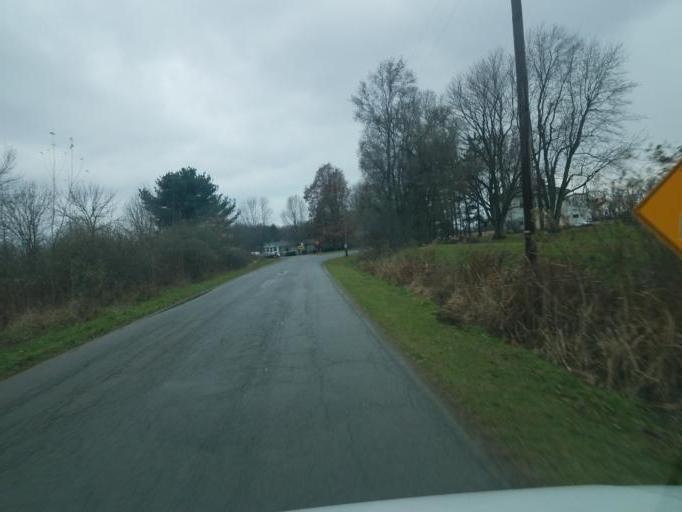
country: US
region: Ohio
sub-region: Richland County
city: Lexington
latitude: 40.6815
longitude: -82.6882
